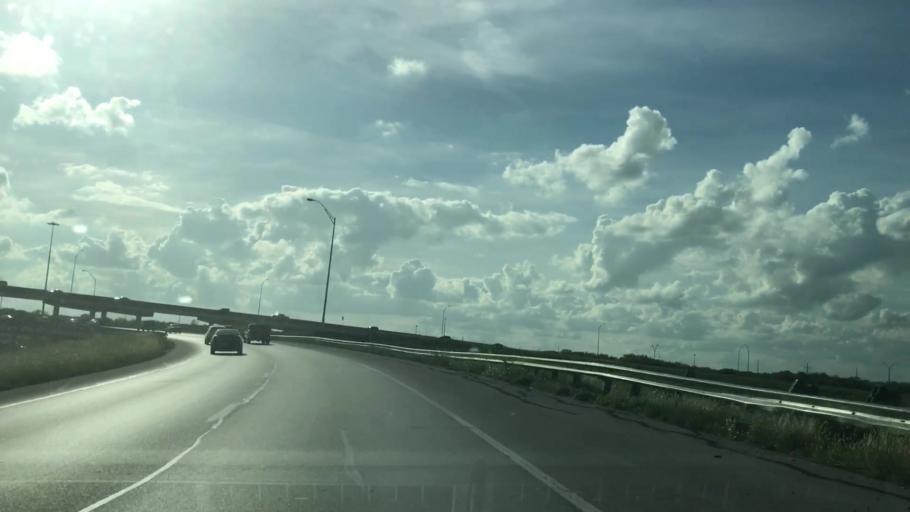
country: US
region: Texas
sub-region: Dallas County
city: Coppell
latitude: 32.9509
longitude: -97.0375
